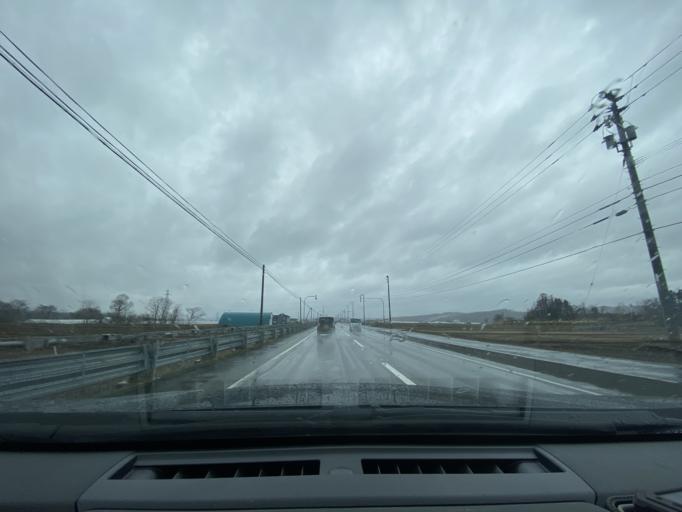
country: JP
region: Hokkaido
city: Fukagawa
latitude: 43.8167
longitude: 141.9955
